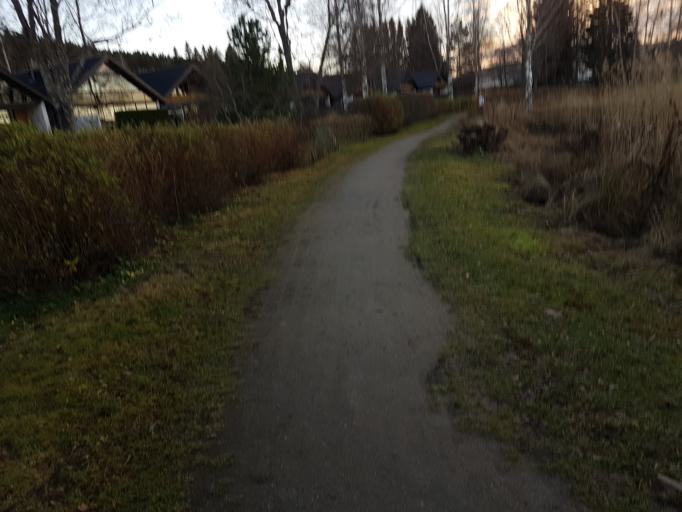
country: FI
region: Northern Savo
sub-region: Kuopio
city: Kuopio
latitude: 62.9352
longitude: 27.6300
